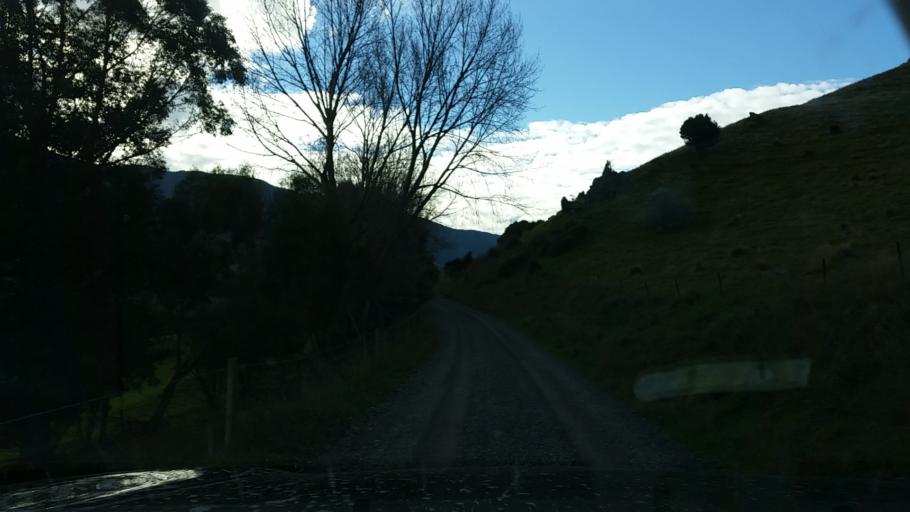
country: NZ
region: Marlborough
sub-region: Marlborough District
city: Blenheim
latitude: -41.7683
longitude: 173.8578
